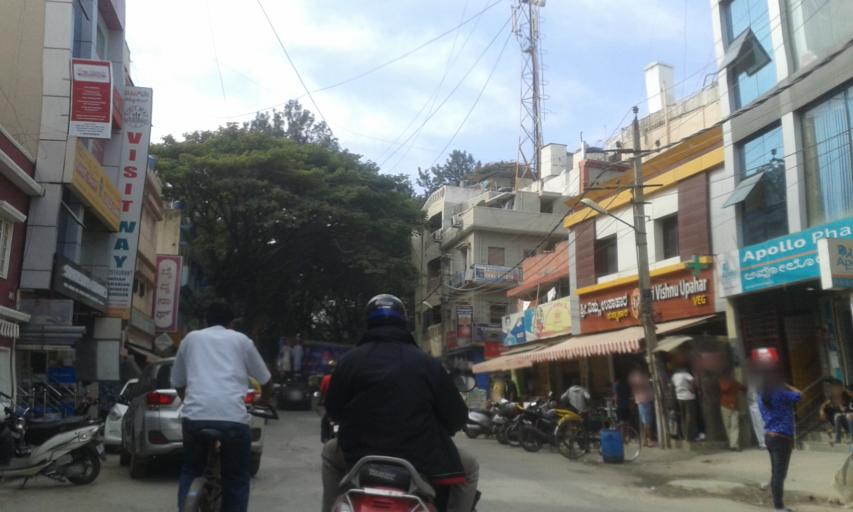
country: IN
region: Karnataka
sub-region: Bangalore Urban
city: Bangalore
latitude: 12.9304
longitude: 77.6338
